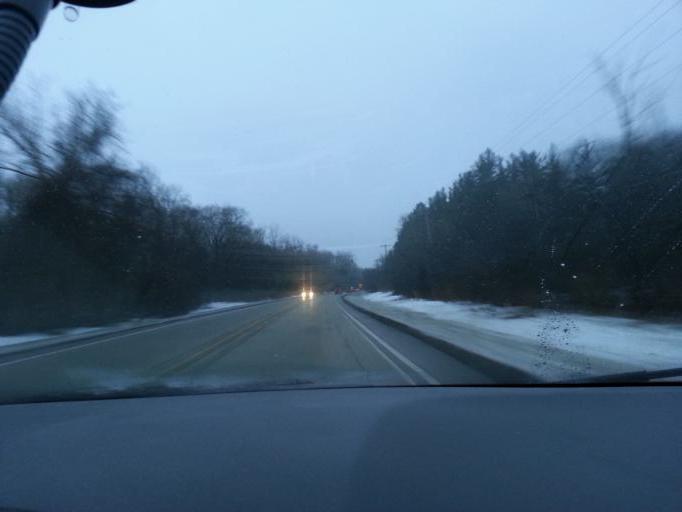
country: US
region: Illinois
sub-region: Kane County
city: Carpentersville
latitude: 42.1216
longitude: -88.2099
